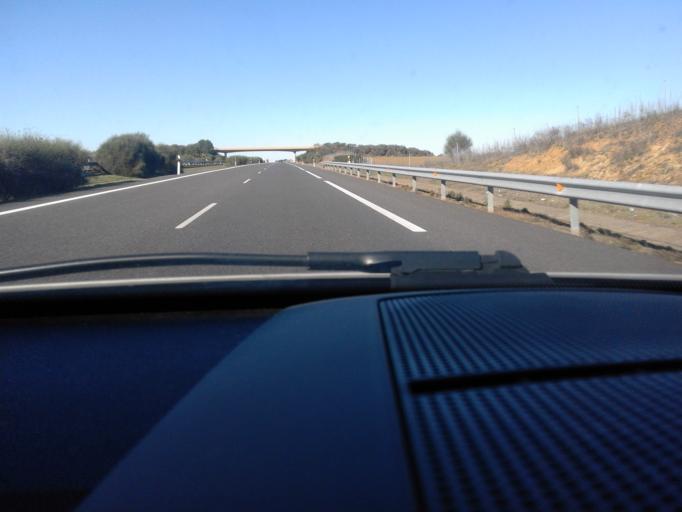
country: ES
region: Castille and Leon
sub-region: Provincia de Leon
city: Villamoratiel de las Matas
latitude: 42.4266
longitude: -5.2941
